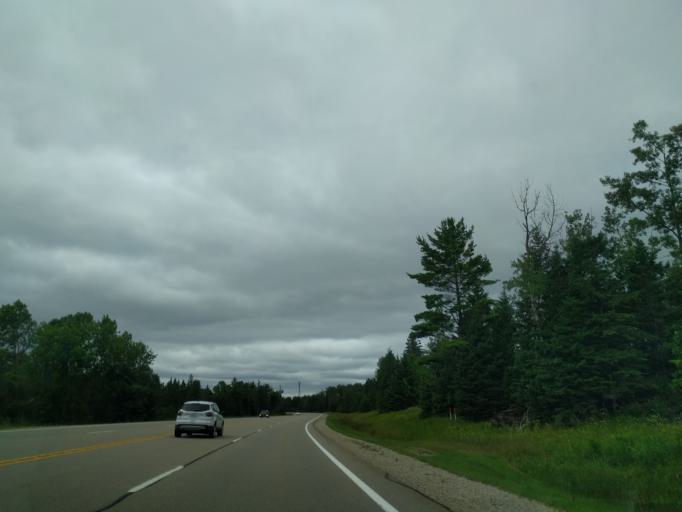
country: US
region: Michigan
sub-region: Delta County
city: Escanaba
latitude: 45.5427
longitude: -87.2754
